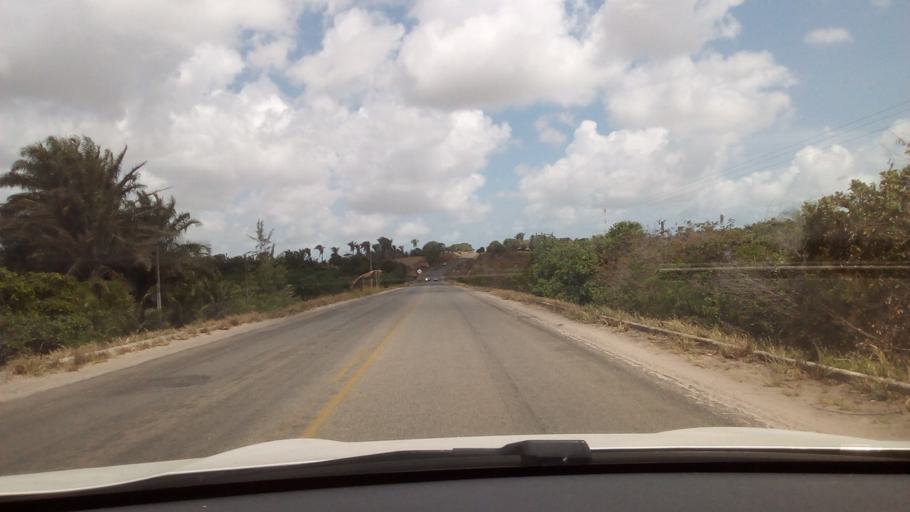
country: BR
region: Paraiba
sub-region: Conde
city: Conde
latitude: -7.2306
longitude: -34.8419
